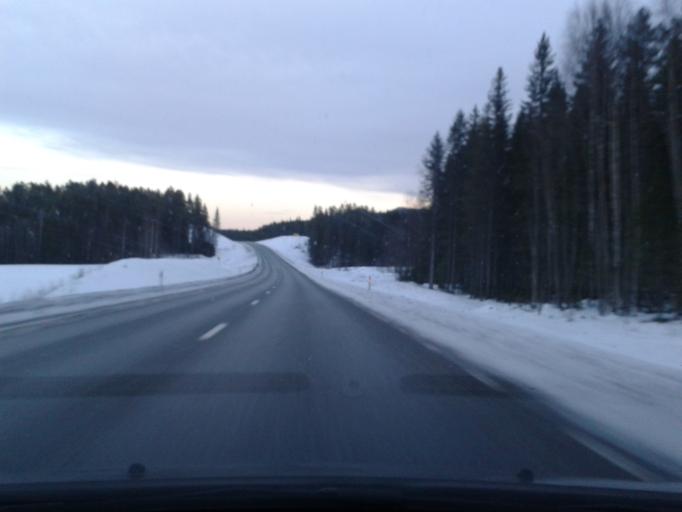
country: SE
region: Vaesternorrland
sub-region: Kramfors Kommun
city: Bollstabruk
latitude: 63.0483
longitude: 17.6248
